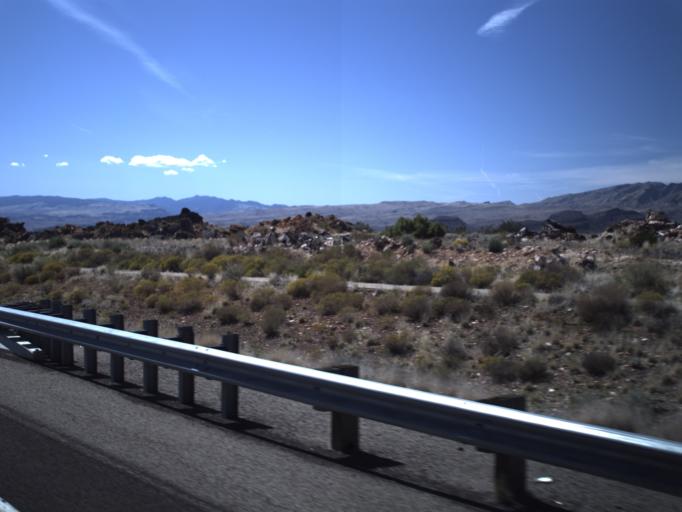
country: US
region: Utah
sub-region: Washington County
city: Santa Clara
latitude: 37.1745
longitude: -113.6189
